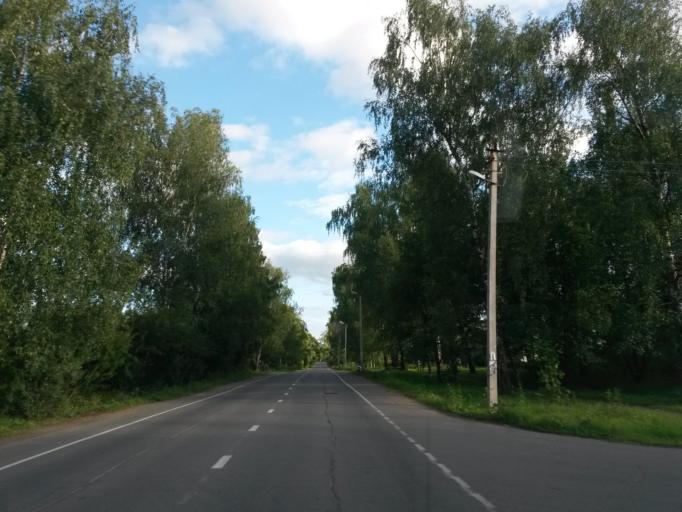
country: RU
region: Jaroslavl
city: Tutayev
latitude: 57.8972
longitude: 39.5271
